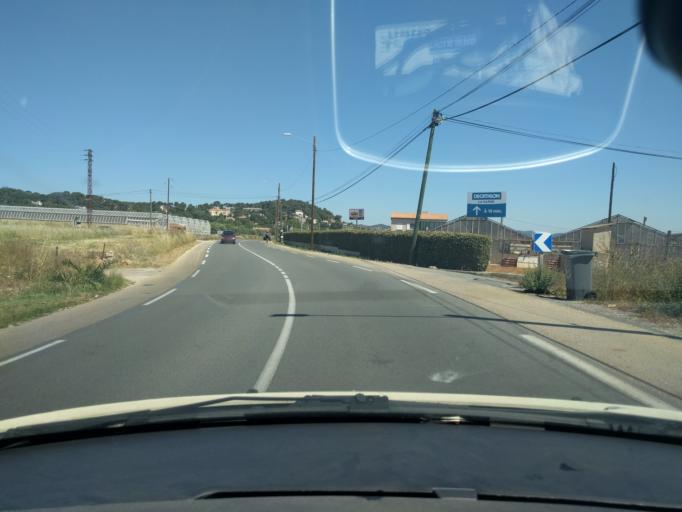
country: FR
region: Provence-Alpes-Cote d'Azur
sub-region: Departement du Var
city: Hyeres
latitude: 43.0857
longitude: 6.1289
